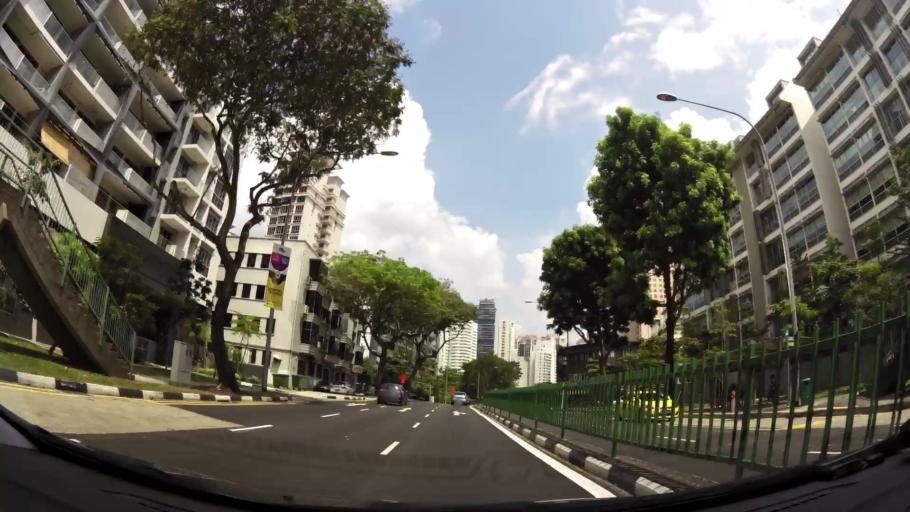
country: SG
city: Singapore
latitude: 1.2950
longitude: 103.8287
